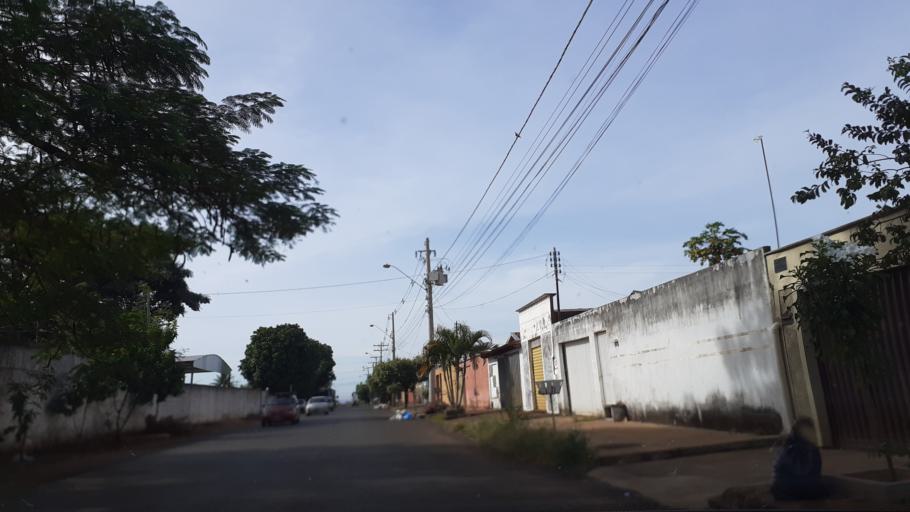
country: BR
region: Goias
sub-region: Itumbiara
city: Itumbiara
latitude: -18.4156
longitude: -49.2423
